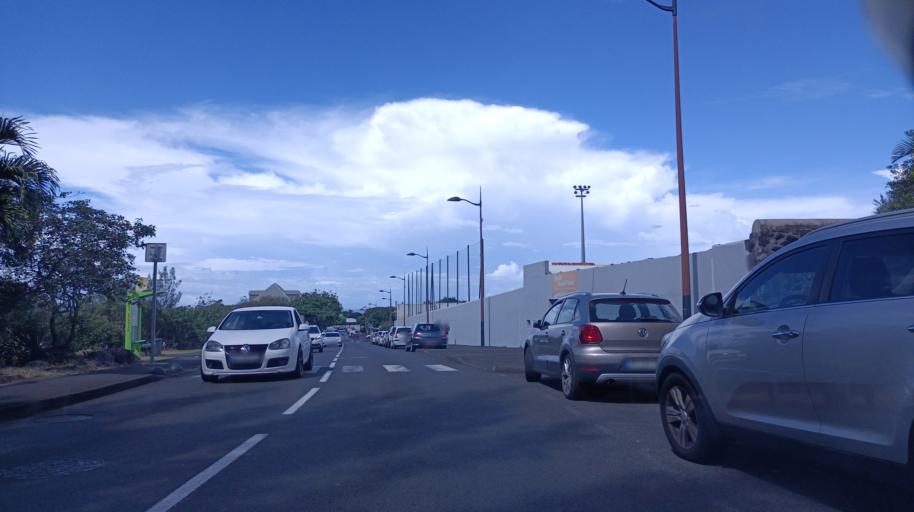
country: RE
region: Reunion
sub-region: Reunion
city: Saint-Joseph
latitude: -21.3777
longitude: 55.6152
